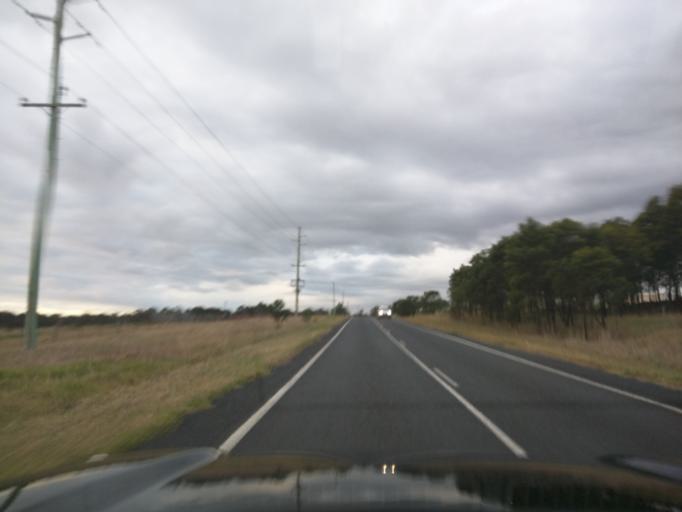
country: AU
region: New South Wales
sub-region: Wollondilly
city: Douglas Park
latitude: -34.2141
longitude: 150.7755
